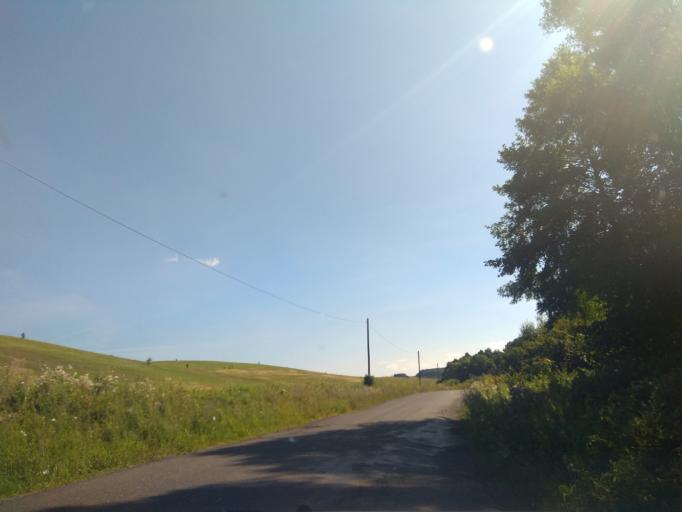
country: HU
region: Heves
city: Szilvasvarad
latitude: 48.1696
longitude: 20.4921
